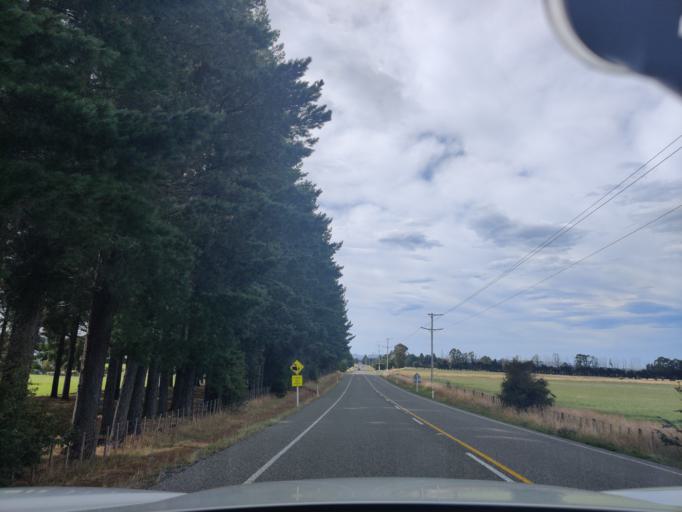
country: NZ
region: Wellington
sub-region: Masterton District
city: Masterton
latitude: -40.8435
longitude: 175.6320
